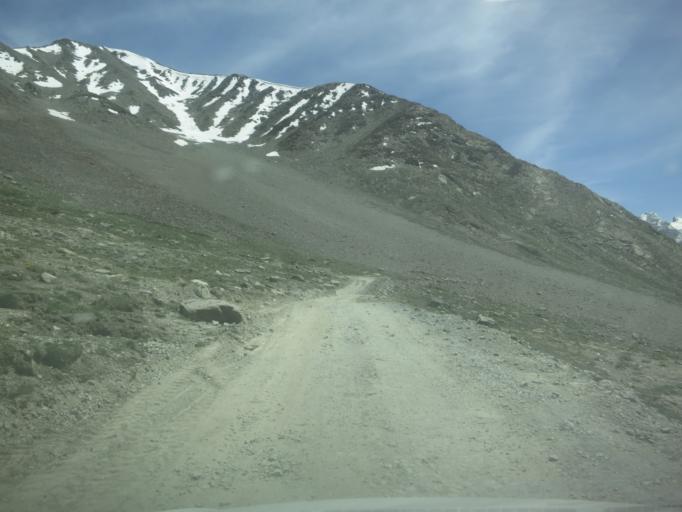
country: IN
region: Himachal Pradesh
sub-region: Kulu
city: Manali
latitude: 32.3901
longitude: 77.6310
